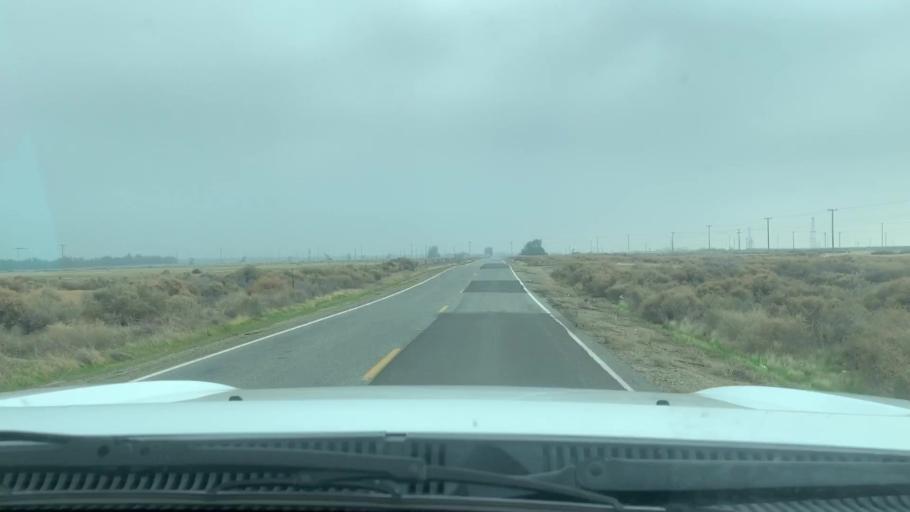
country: US
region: California
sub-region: Kern County
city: Lost Hills
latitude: 35.5464
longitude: -119.7834
